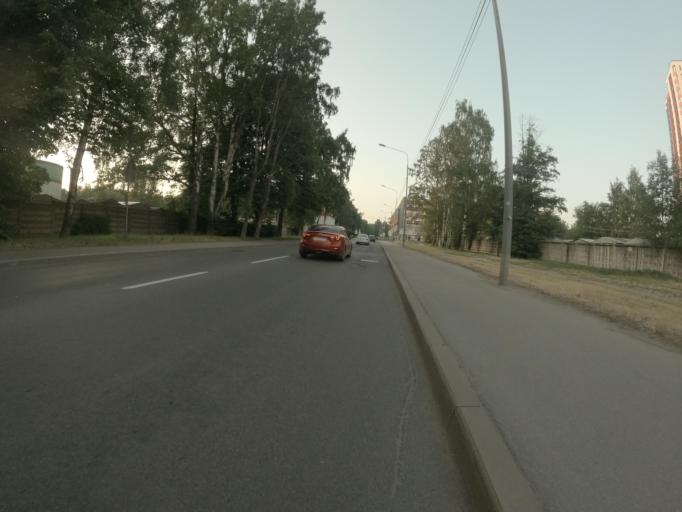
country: RU
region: Leningrad
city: Kalininskiy
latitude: 59.9854
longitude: 30.3907
